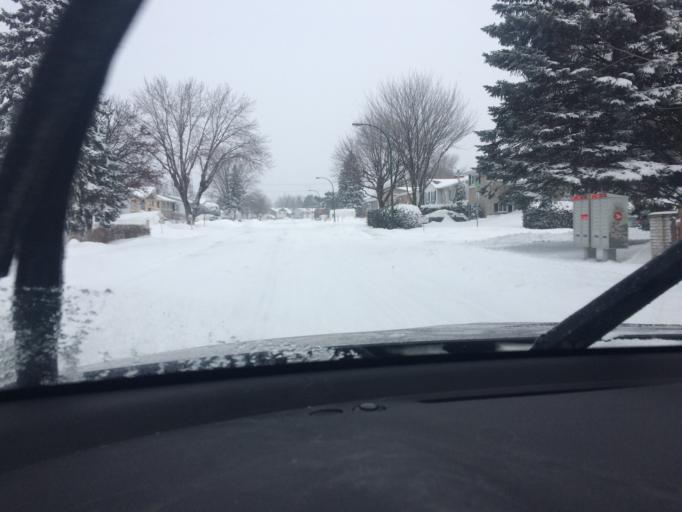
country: CA
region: Quebec
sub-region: Monteregie
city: Brossard
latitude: 45.4679
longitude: -73.4591
